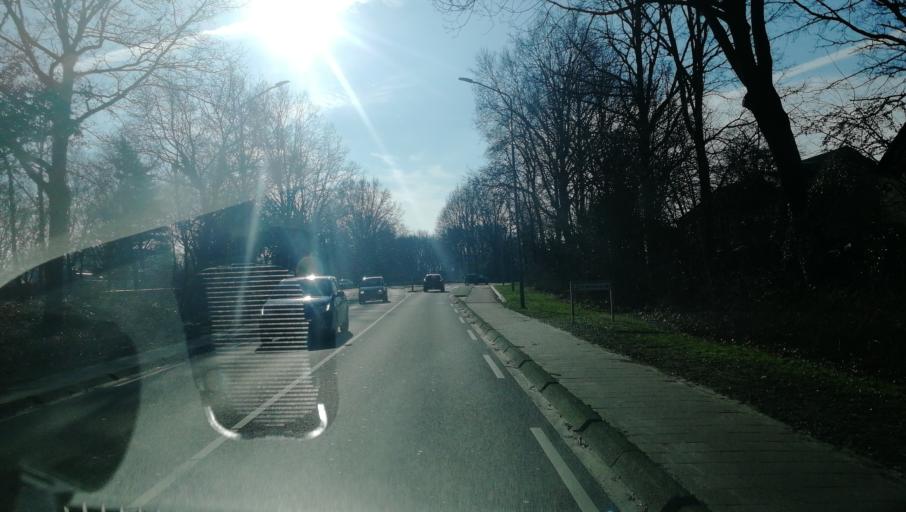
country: NL
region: Limburg
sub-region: Gemeente Venlo
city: Tegelen
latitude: 51.3688
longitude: 6.1358
